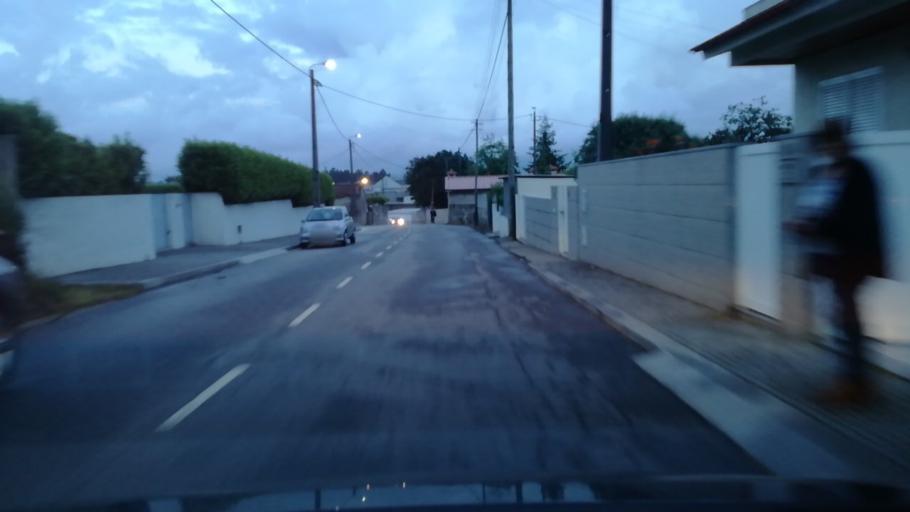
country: PT
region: Porto
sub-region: Maia
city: Maia
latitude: 41.2506
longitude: -8.6248
